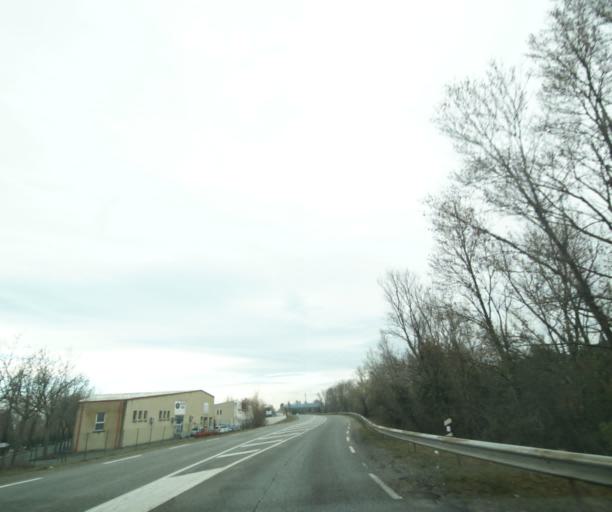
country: FR
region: Rhone-Alpes
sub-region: Departement de la Drome
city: Valence
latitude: 44.9378
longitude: 4.8888
